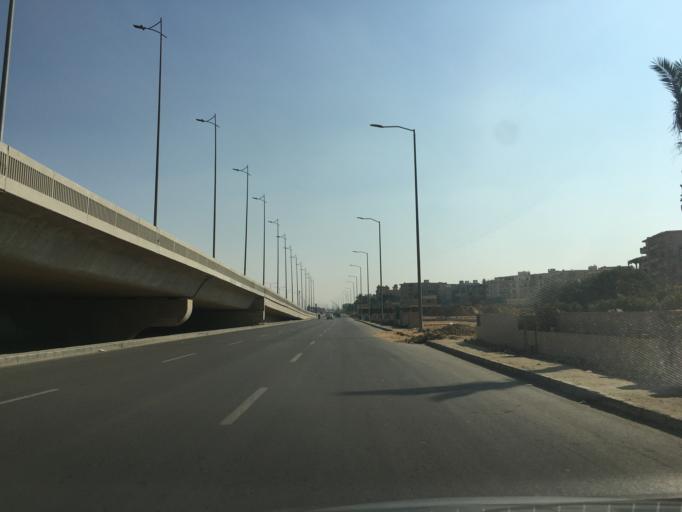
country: EG
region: Al Jizah
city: Awsim
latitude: 30.0068
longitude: 30.9830
